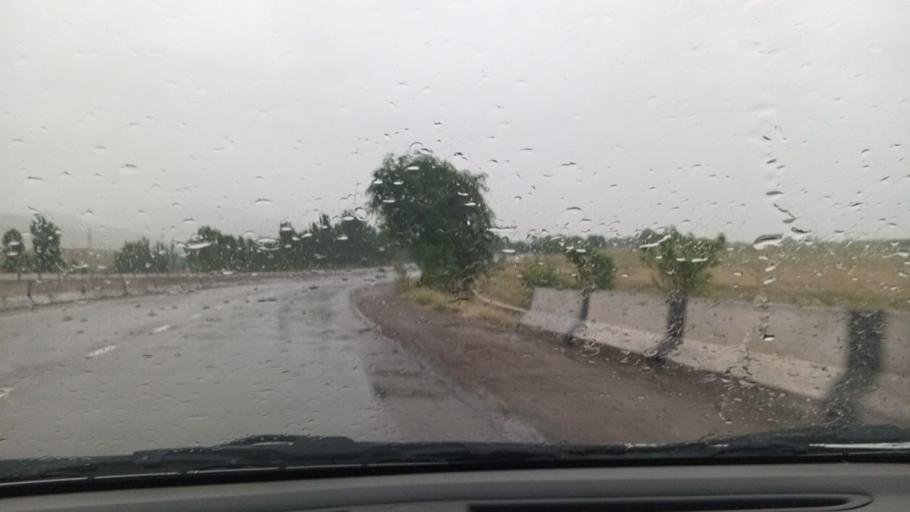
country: UZ
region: Toshkent
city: Angren
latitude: 40.9457
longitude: 69.9075
